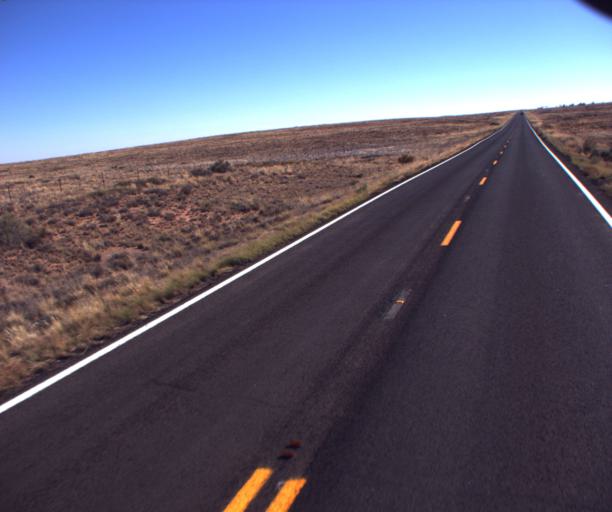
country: US
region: Arizona
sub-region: Coconino County
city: Tuba City
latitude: 35.9686
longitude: -110.9583
